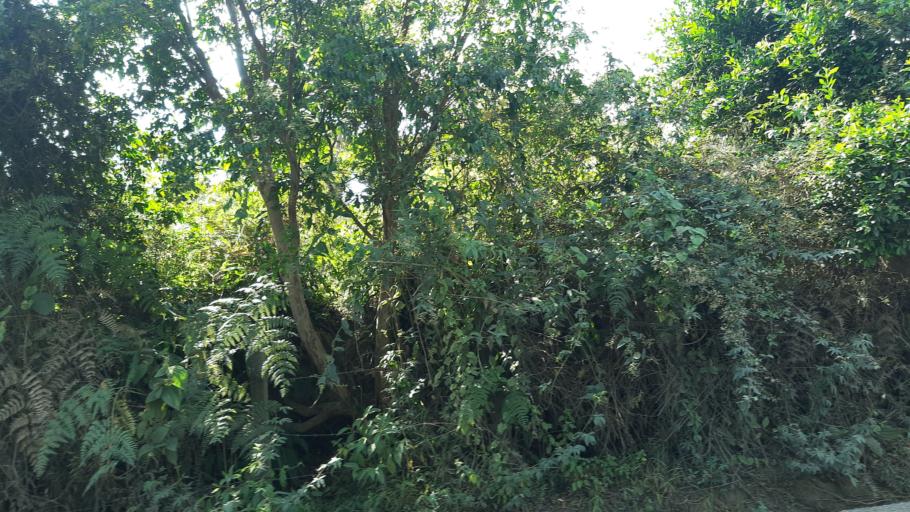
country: CO
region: Boyaca
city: Moniquira
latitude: 5.7963
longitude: -73.6021
